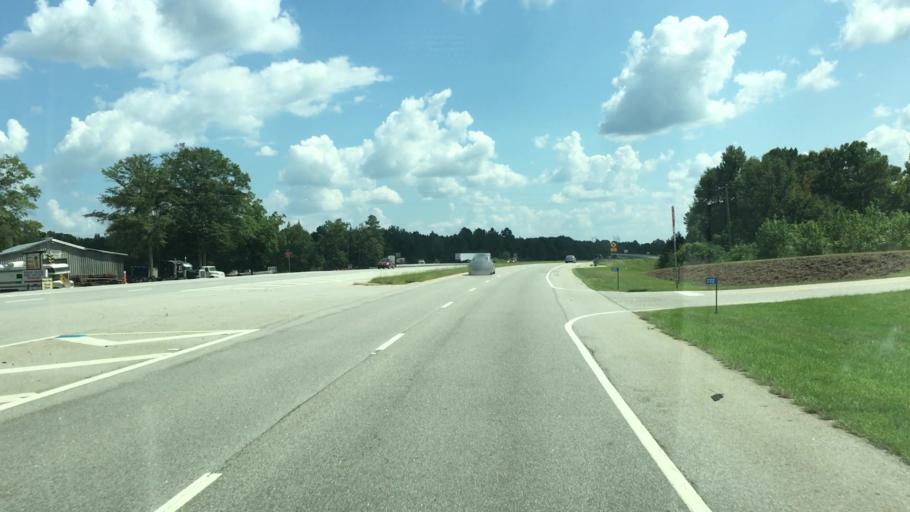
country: US
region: Georgia
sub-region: Putnam County
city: Eatonton
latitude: 33.2857
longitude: -83.3714
